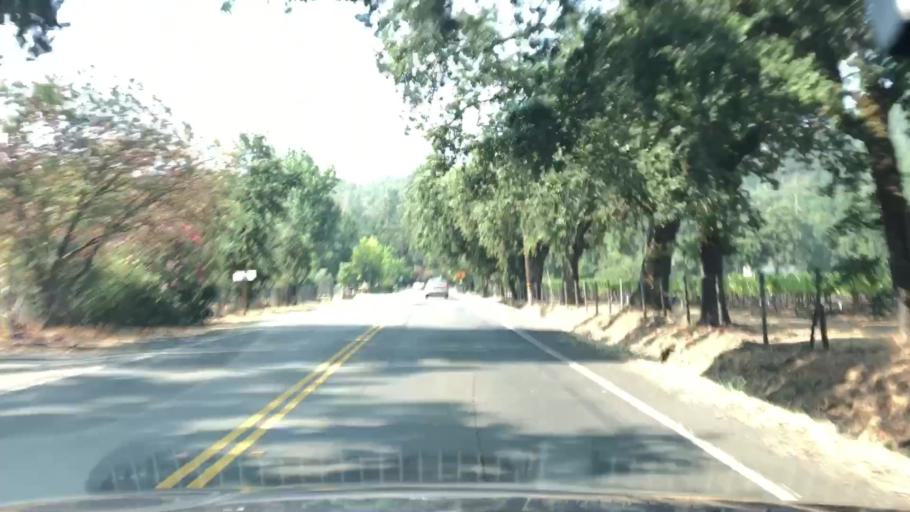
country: US
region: California
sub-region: Napa County
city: Calistoga
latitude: 38.5906
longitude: -122.6056
